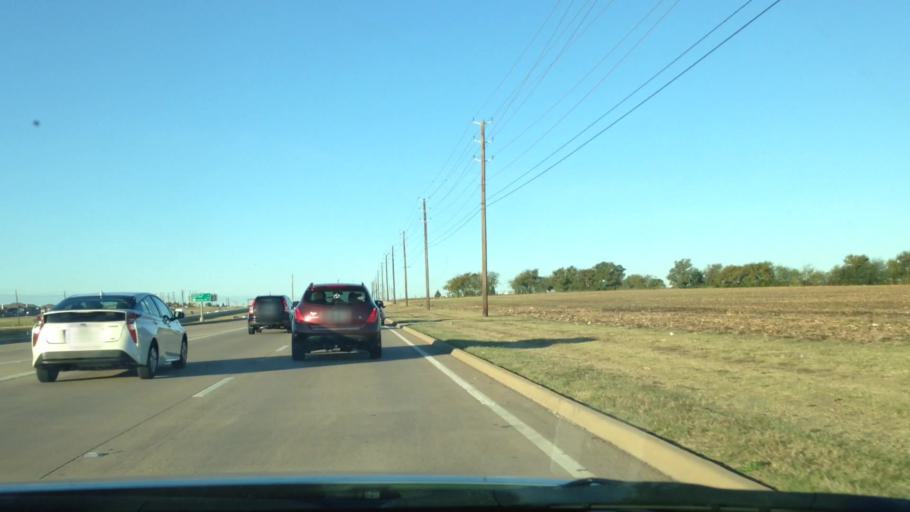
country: US
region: Texas
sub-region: Collin County
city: Frisco
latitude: 33.1175
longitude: -96.7562
